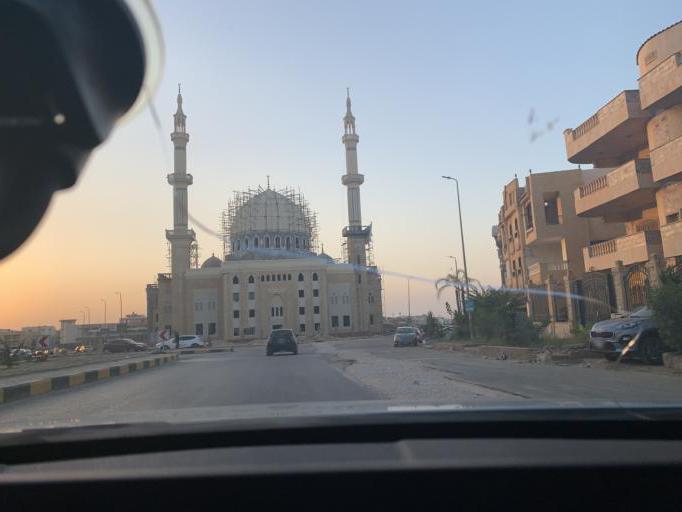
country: EG
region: Muhafazat al Qahirah
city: Cairo
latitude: 30.0047
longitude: 31.4577
